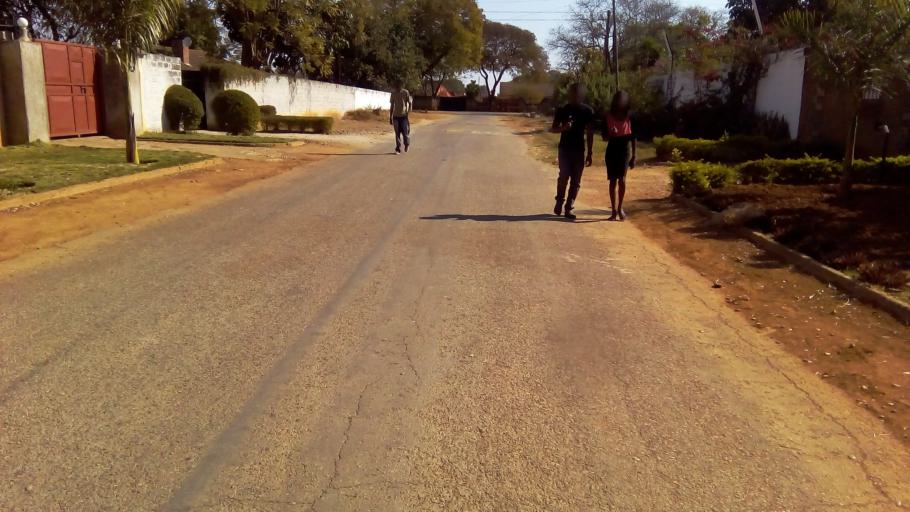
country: ZM
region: Lusaka
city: Lusaka
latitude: -15.4433
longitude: 28.3488
